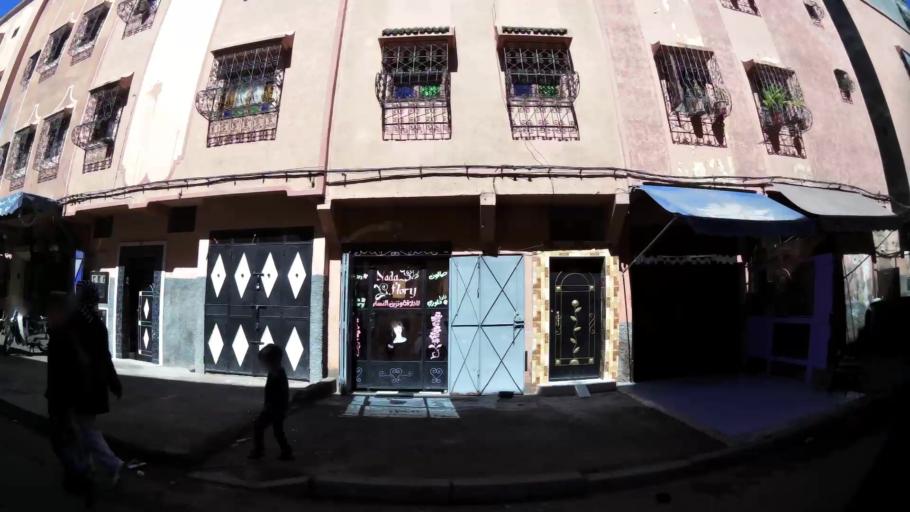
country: MA
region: Marrakech-Tensift-Al Haouz
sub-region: Marrakech
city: Marrakesh
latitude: 31.6489
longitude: -7.9838
